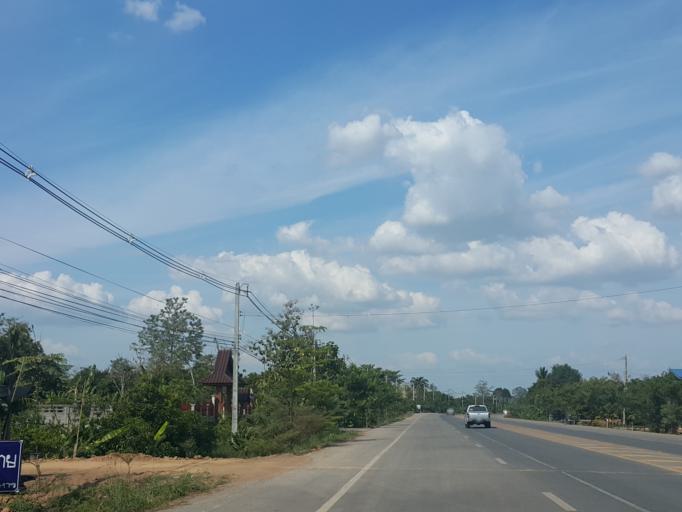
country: TH
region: Sukhothai
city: Si Samrong
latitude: 17.2347
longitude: 99.8462
